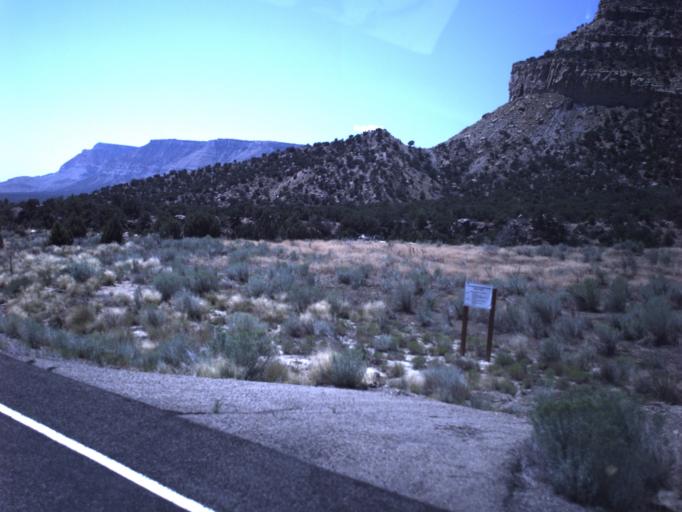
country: US
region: Utah
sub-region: Emery County
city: Orangeville
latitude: 39.3053
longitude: -111.1194
